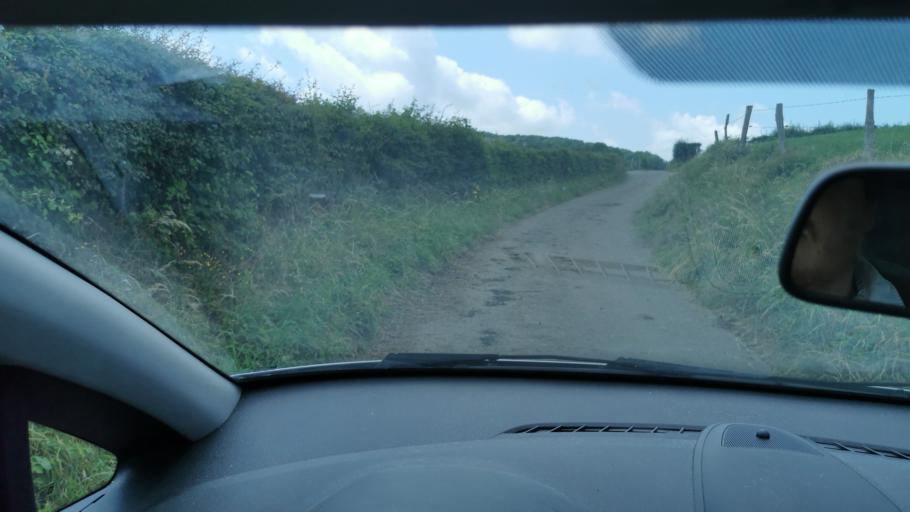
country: BE
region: Wallonia
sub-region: Province de Liege
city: Theux
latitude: 50.5373
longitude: 5.7923
